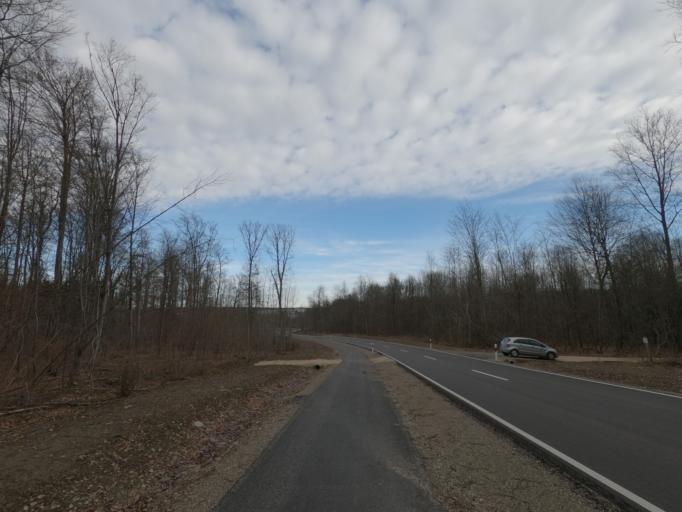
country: DE
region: Baden-Wuerttemberg
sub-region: Regierungsbezirk Stuttgart
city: Schlierbach
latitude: 48.6650
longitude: 9.5288
